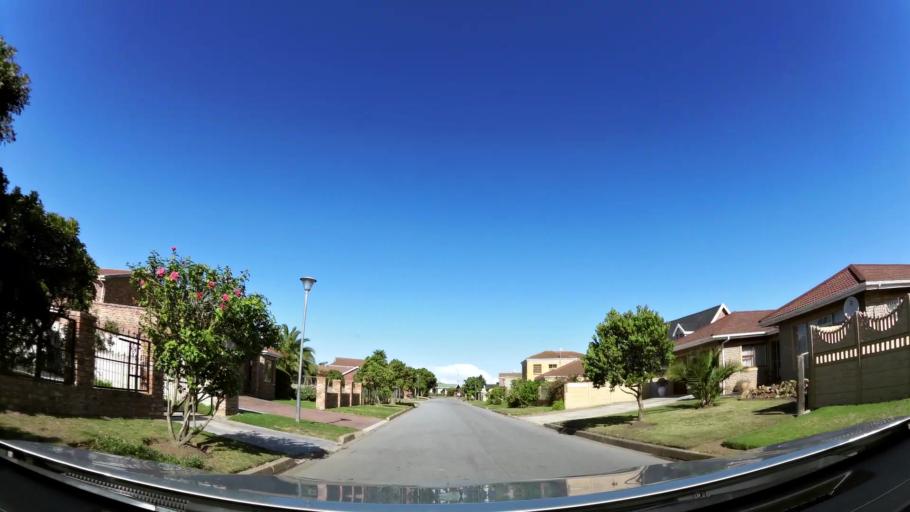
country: ZA
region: Western Cape
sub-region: Eden District Municipality
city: George
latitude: -33.9846
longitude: 22.4375
